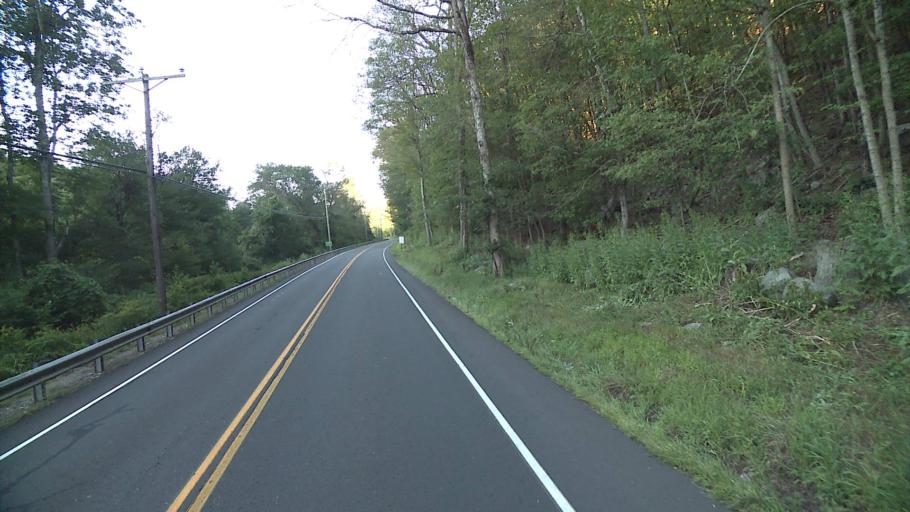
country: US
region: Connecticut
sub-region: Tolland County
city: Stafford Springs
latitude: 41.9414
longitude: -72.3065
